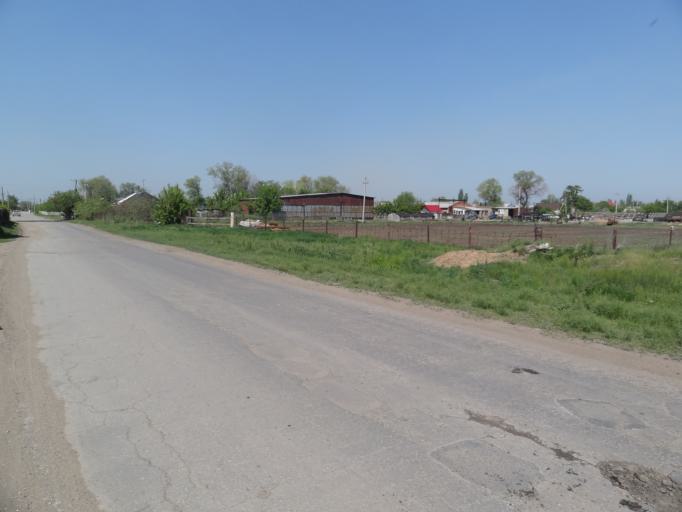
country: RU
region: Saratov
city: Privolzhskiy
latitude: 51.4079
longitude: 46.1044
